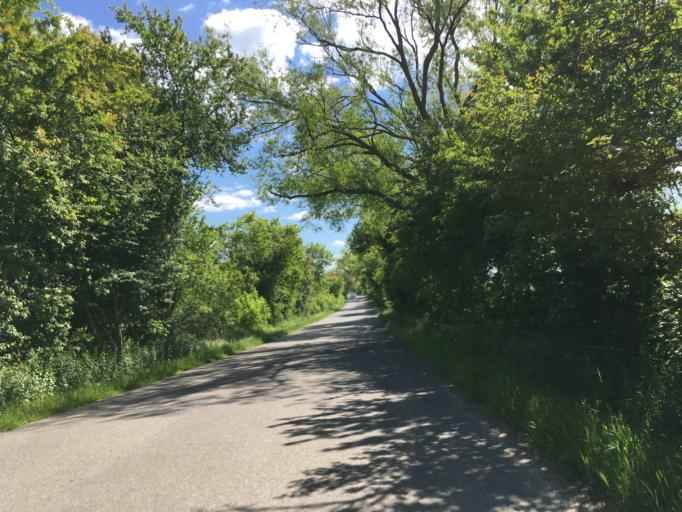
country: DE
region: Brandenburg
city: Rudnitz
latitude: 52.7064
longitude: 13.6617
